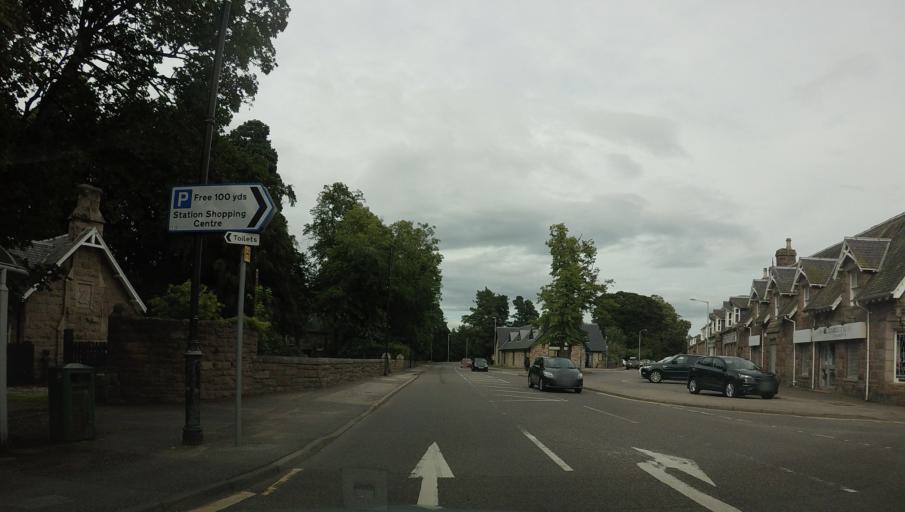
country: GB
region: Scotland
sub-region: Aberdeenshire
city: Aboyne
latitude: 57.0767
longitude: -2.7792
